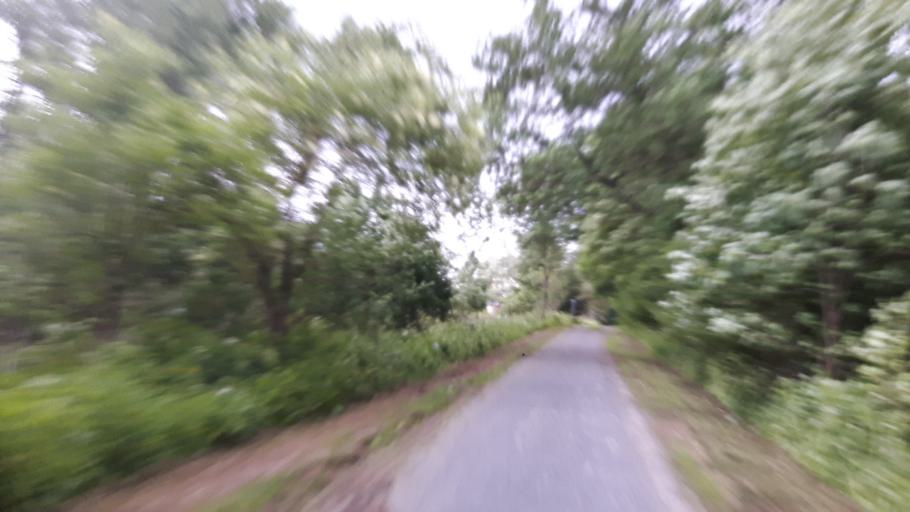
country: DE
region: Thuringia
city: Bad Berka
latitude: 50.8841
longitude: 11.2720
